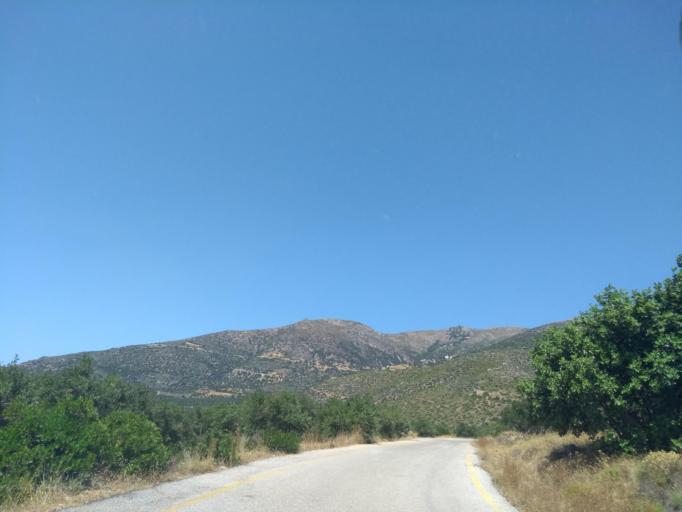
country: GR
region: Crete
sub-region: Nomos Chanias
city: Vryses
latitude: 35.3598
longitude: 23.5408
